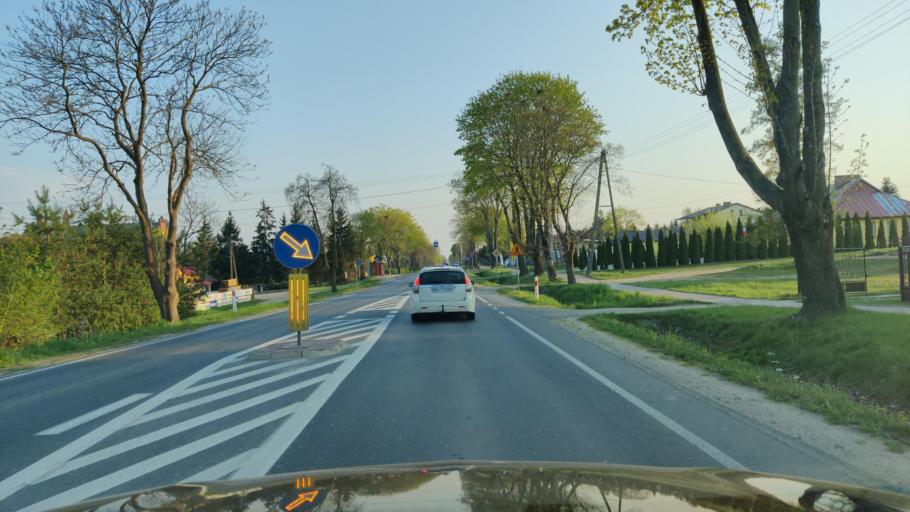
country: PL
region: Masovian Voivodeship
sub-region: Powiat legionowski
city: Serock
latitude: 52.5712
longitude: 21.0898
